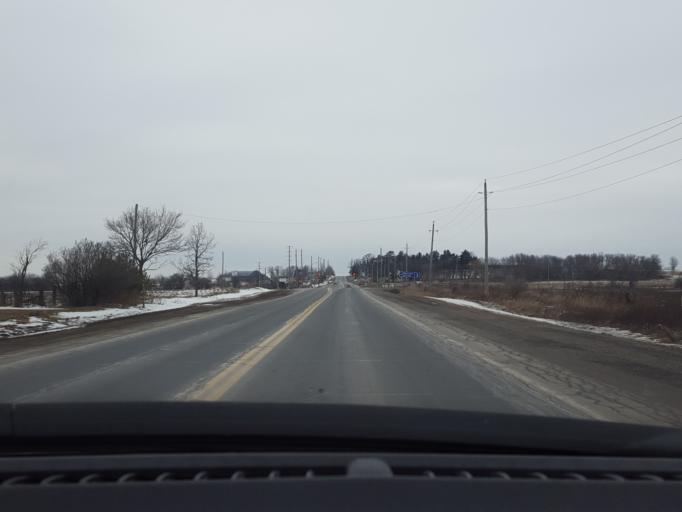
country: CA
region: Ontario
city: Newmarket
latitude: 44.1406
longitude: -79.4251
